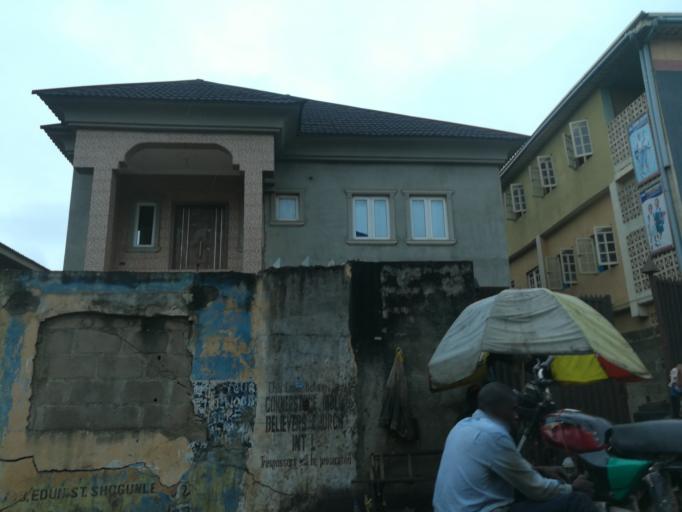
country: NG
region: Lagos
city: Oshodi
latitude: 6.5677
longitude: 3.3395
